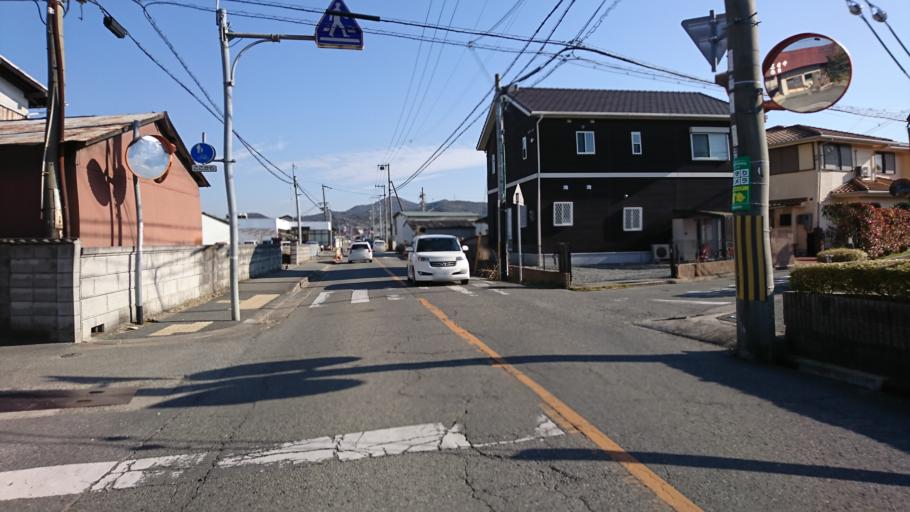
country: JP
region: Hyogo
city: Kakogawacho-honmachi
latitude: 34.8161
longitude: 134.8256
